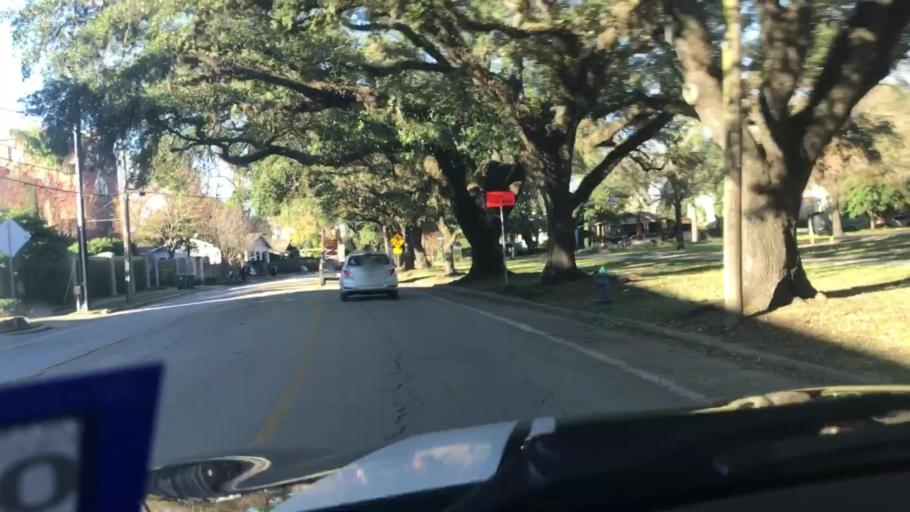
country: US
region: Texas
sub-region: Harris County
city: Houston
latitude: 29.7829
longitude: -95.3719
